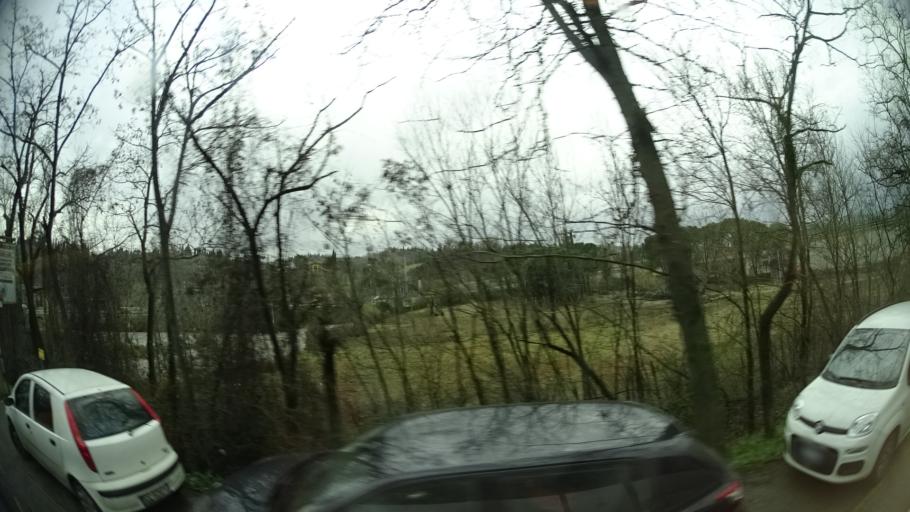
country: IT
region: Tuscany
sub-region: Province of Florence
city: Tavarnuzze
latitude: 43.7228
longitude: 11.2270
